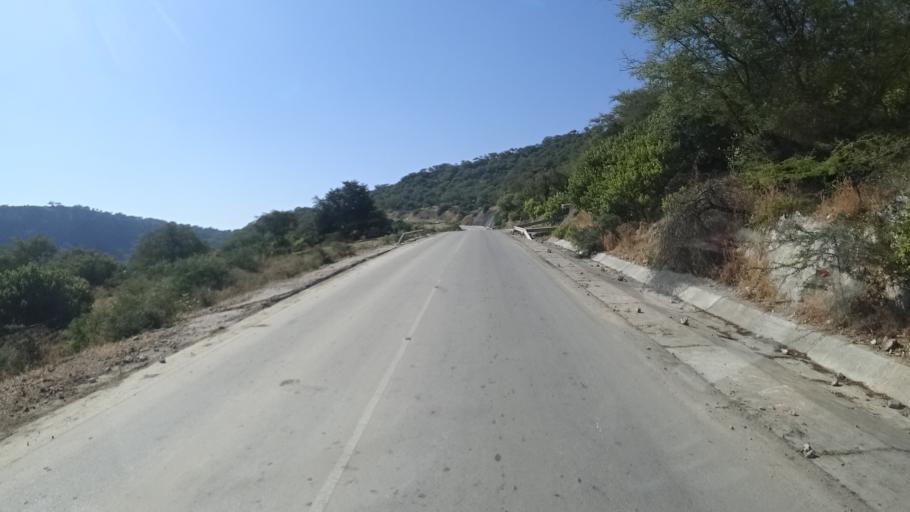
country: OM
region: Zufar
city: Salalah
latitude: 17.0600
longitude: 54.6113
